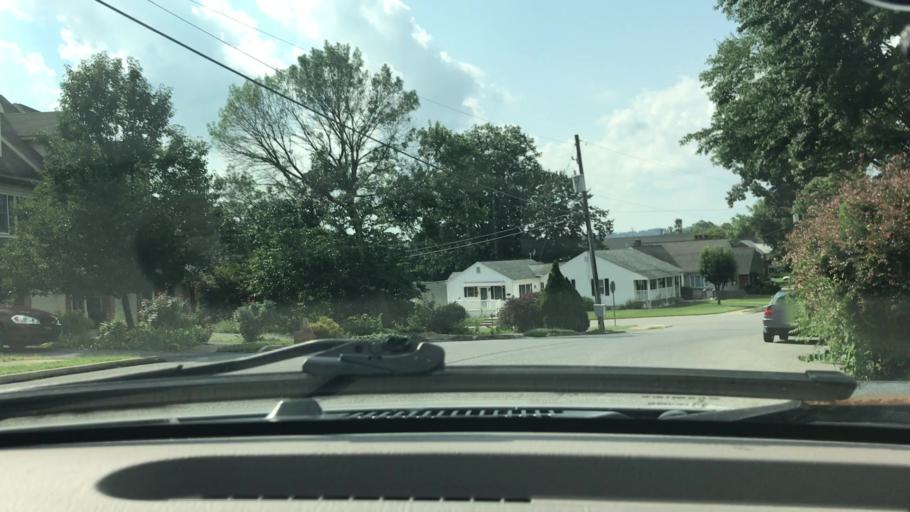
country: US
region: Pennsylvania
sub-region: Lancaster County
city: Elizabethtown
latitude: 40.1447
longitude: -76.5984
